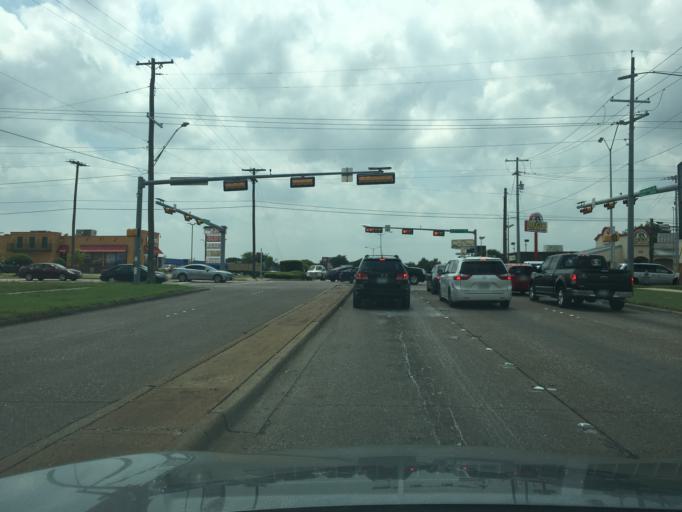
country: US
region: Texas
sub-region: Dallas County
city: Richardson
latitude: 32.9166
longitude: -96.6998
